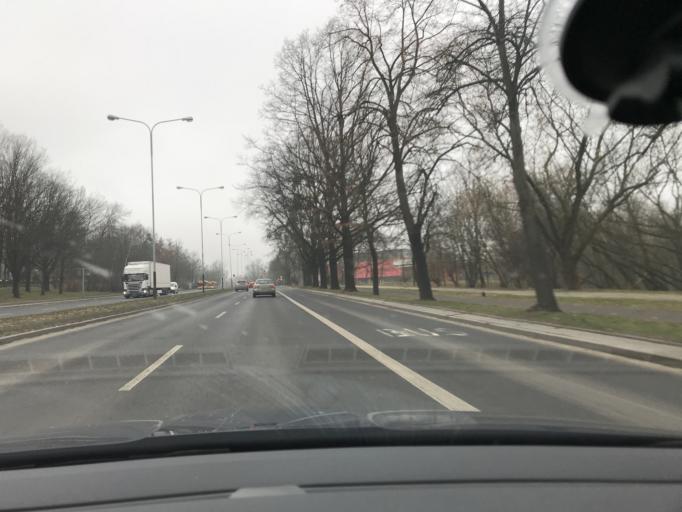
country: PL
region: Lodz Voivodeship
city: Lodz
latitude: 51.7899
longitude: 19.4863
